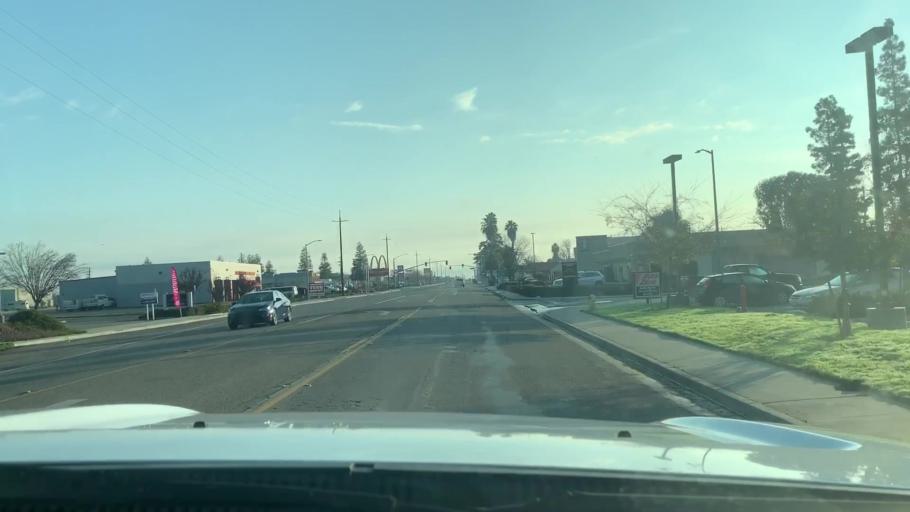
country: US
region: California
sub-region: Kern County
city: Wasco
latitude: 35.6015
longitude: -119.3519
